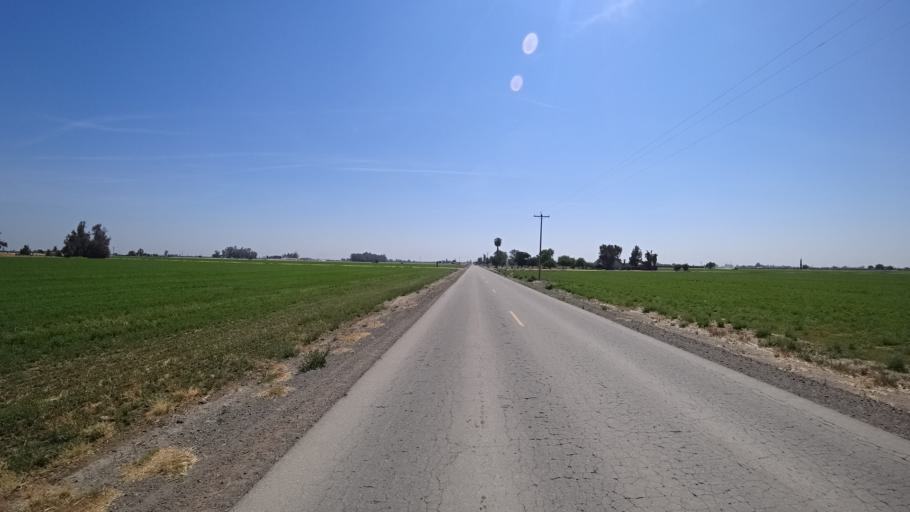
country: US
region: California
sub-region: Fresno County
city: Riverdale
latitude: 36.4022
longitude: -119.8573
